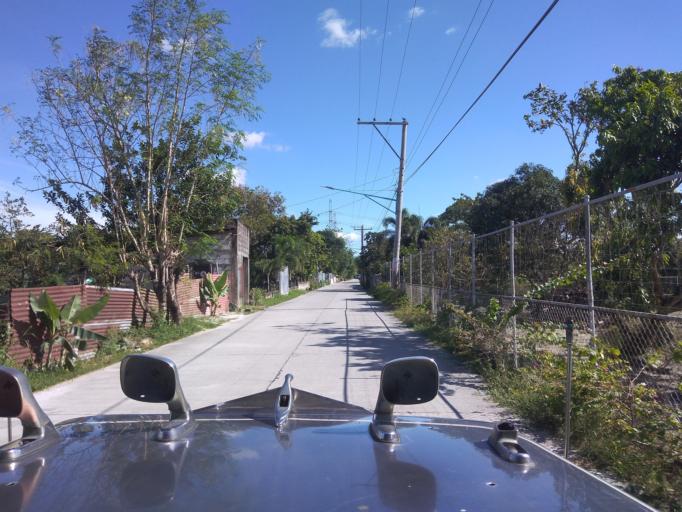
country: PH
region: Central Luzon
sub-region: Province of Pampanga
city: Bacolor
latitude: 15.0075
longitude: 120.6466
